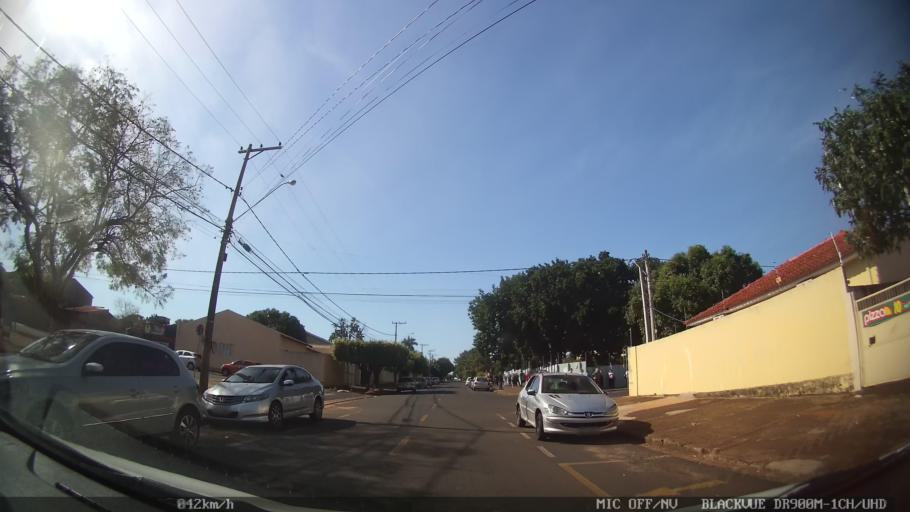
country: BR
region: Sao Paulo
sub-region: Sao Jose Do Rio Preto
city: Sao Jose do Rio Preto
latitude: -20.7897
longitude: -49.4047
